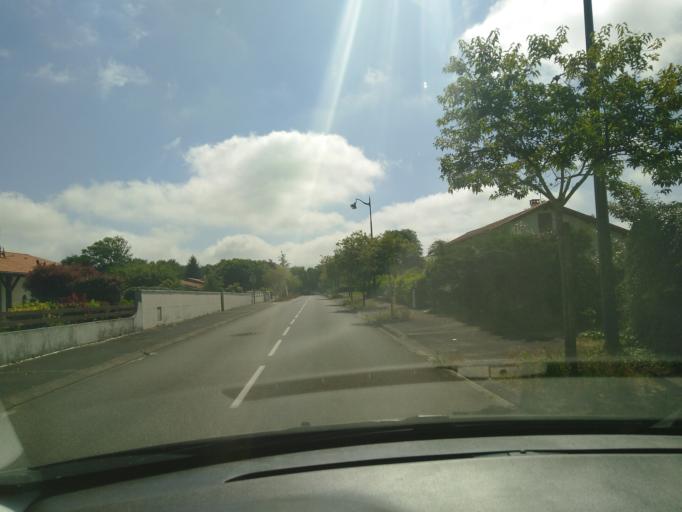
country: FR
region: Aquitaine
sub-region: Departement des Landes
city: Saint-Vincent-de-Paul
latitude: 43.7846
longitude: -0.9883
